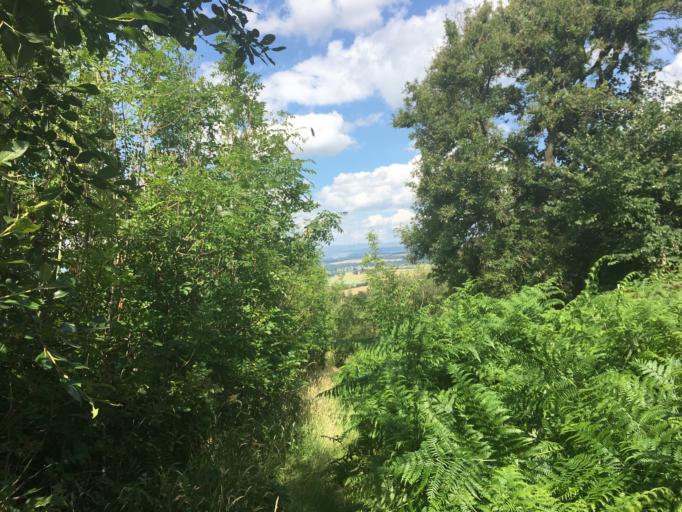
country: GB
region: Scotland
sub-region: Stirling
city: Stirling
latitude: 56.1025
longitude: -3.9827
